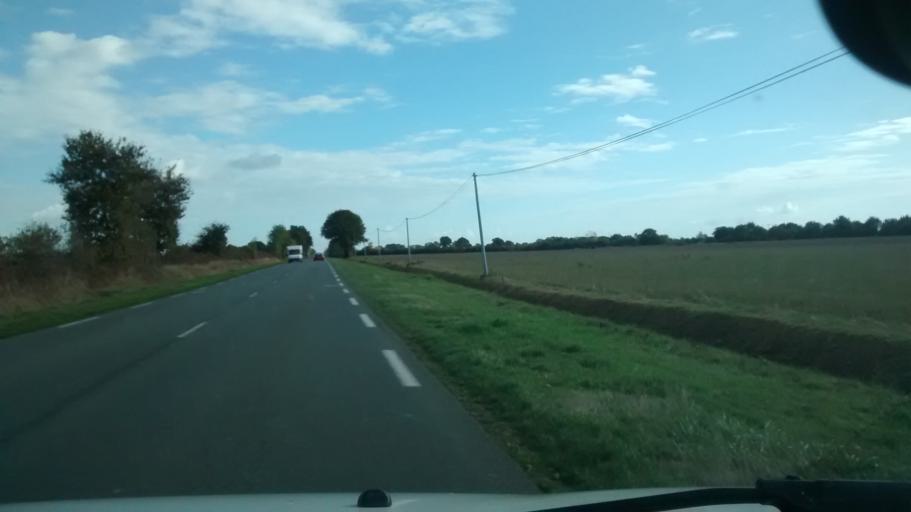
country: FR
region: Pays de la Loire
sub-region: Departement de Maine-et-Loire
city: Pouance
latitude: 47.7443
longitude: -1.2233
